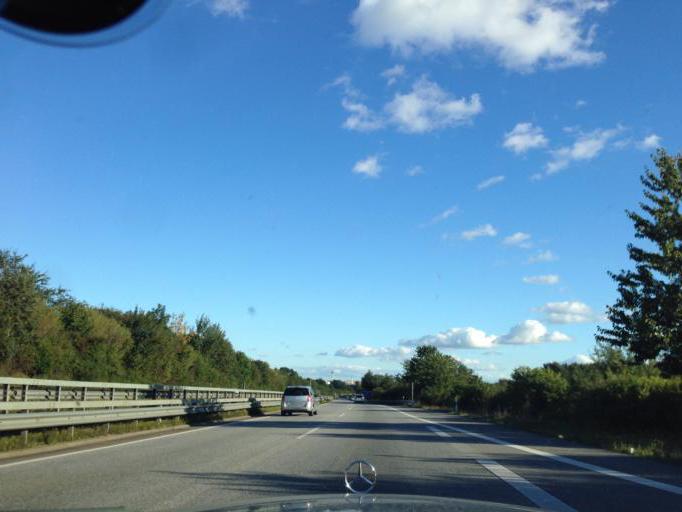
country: DE
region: Schleswig-Holstein
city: Schackendorf
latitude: 53.9569
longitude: 10.2650
